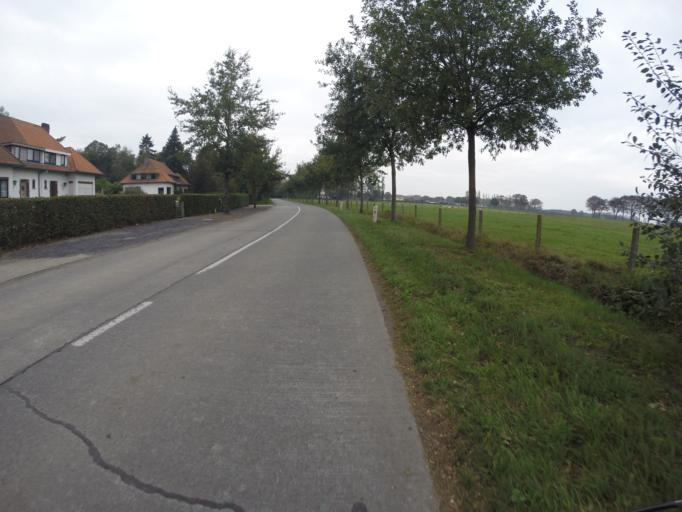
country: BE
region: Flanders
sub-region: Provincie West-Vlaanderen
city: Beernem
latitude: 51.0831
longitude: 3.3484
